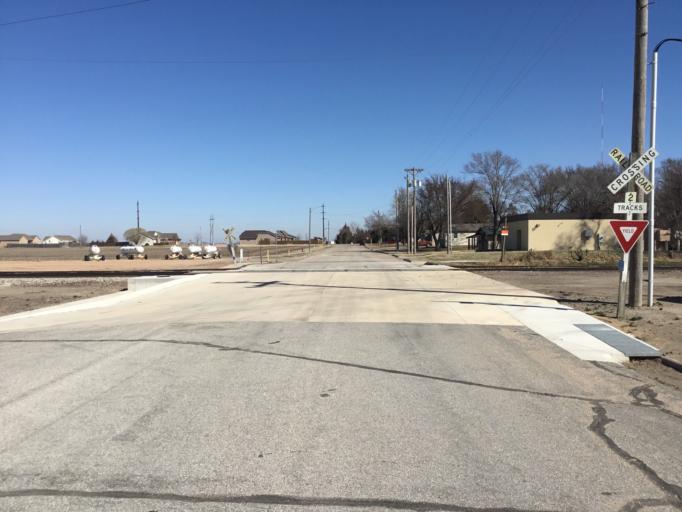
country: US
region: Kansas
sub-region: Sedgwick County
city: Colwich
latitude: 37.7841
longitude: -97.5397
